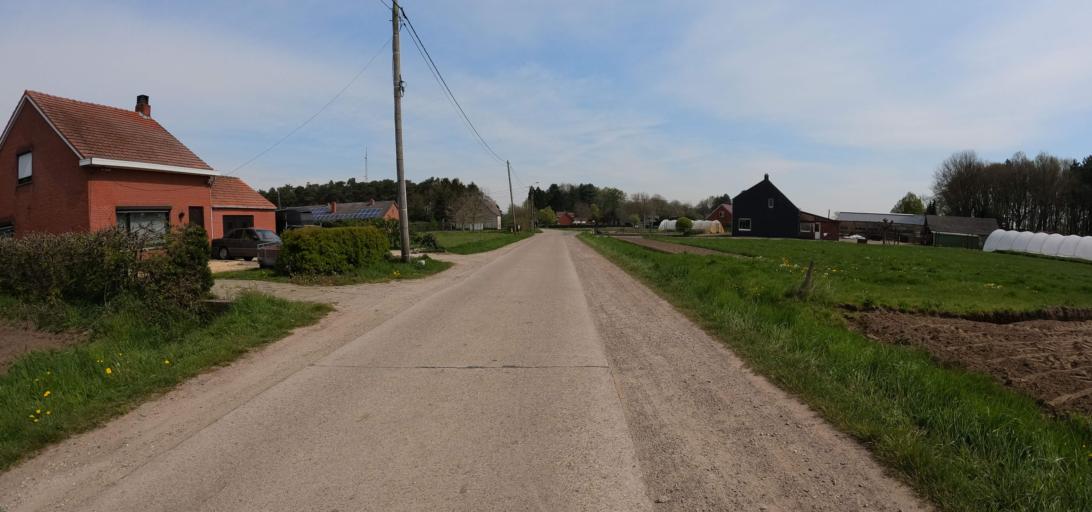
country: BE
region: Flanders
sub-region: Provincie Antwerpen
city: Zoersel
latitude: 51.2261
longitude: 4.7091
